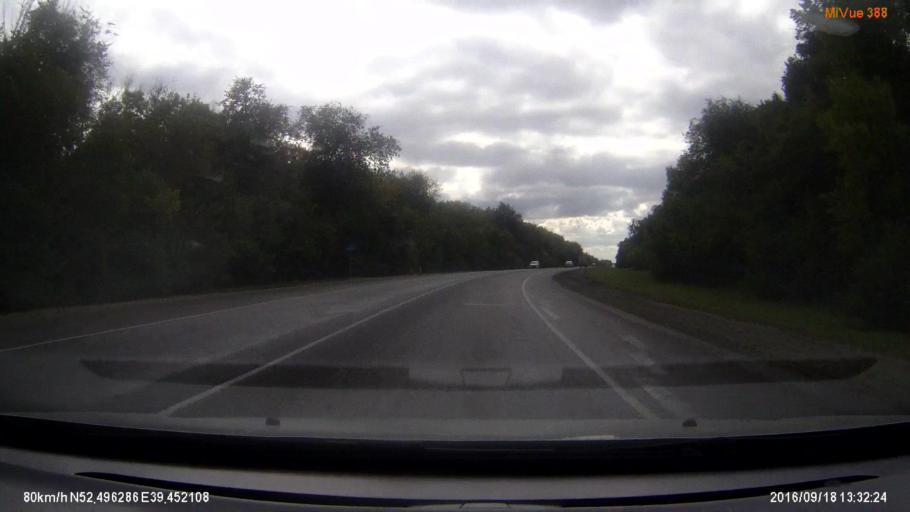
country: RU
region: Lipetsk
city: Borinskoye
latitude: 52.4689
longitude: 39.4181
